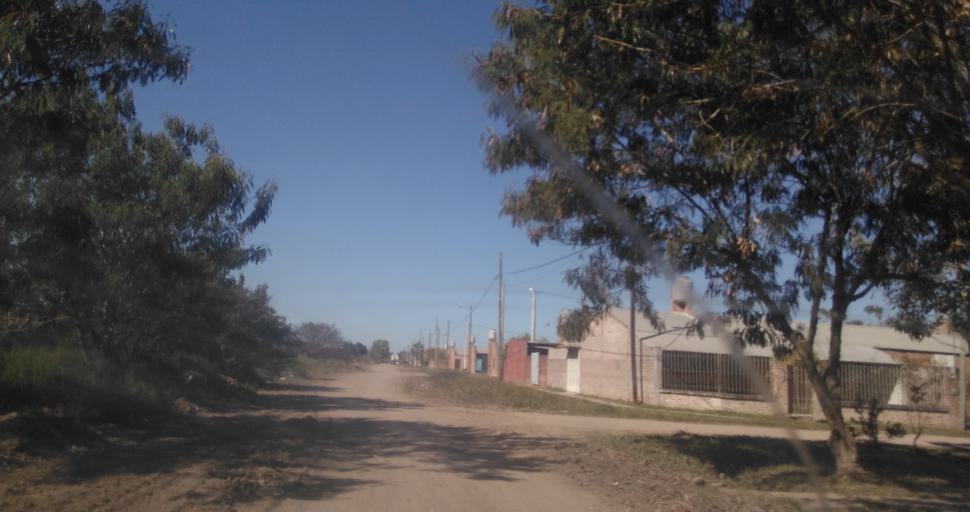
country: AR
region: Chaco
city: Fontana
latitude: -27.4566
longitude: -59.0438
